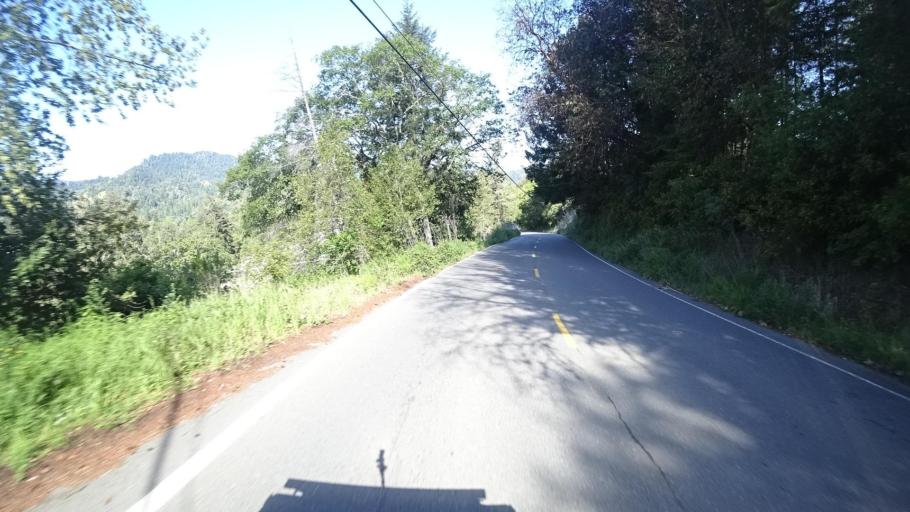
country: US
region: California
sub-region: Humboldt County
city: Redway
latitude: 40.1053
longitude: -123.7889
